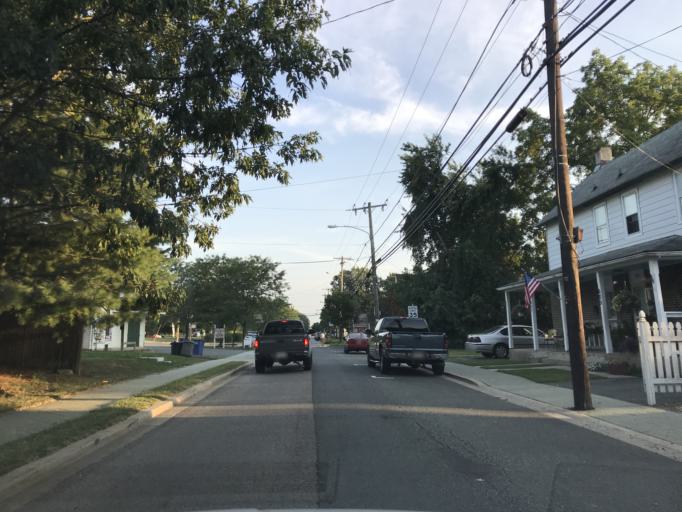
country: US
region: Maryland
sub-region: Cecil County
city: North East
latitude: 39.5943
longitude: -75.9414
